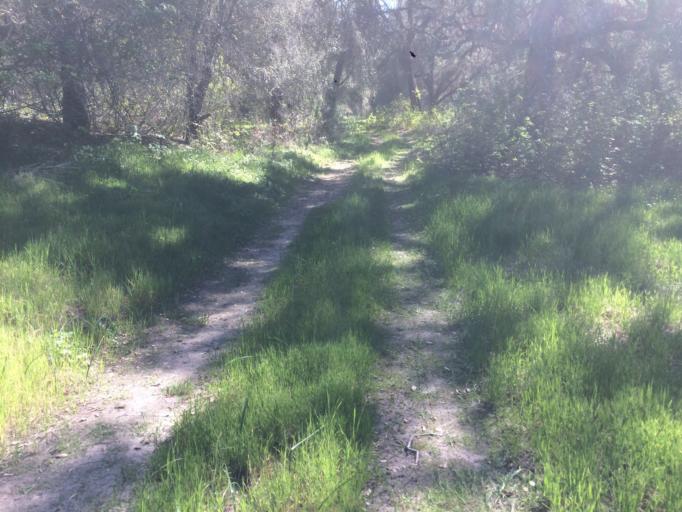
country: US
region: California
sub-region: San Luis Obispo County
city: Nipomo
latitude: 35.1785
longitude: -120.3931
